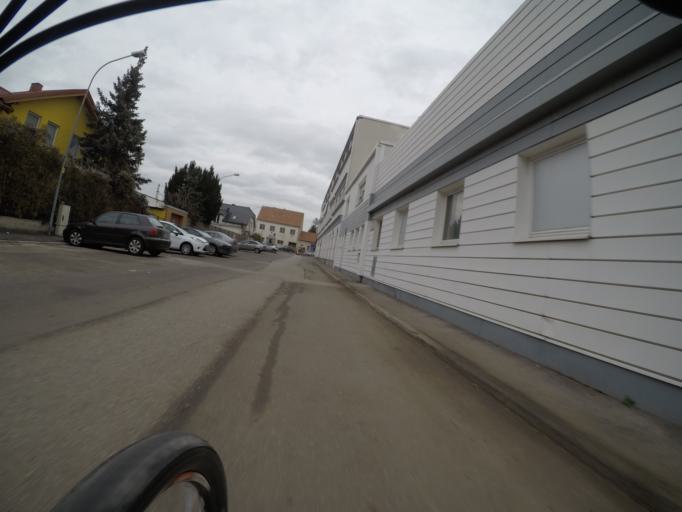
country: AT
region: Lower Austria
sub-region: Politischer Bezirk Modling
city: Vosendorf
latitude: 48.1242
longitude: 16.3210
